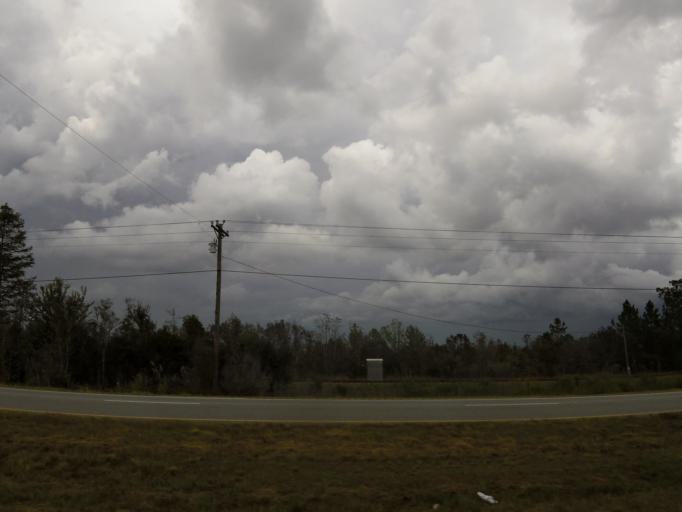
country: US
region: Georgia
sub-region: Brantley County
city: Nahunta
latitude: 31.2062
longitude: -81.9666
